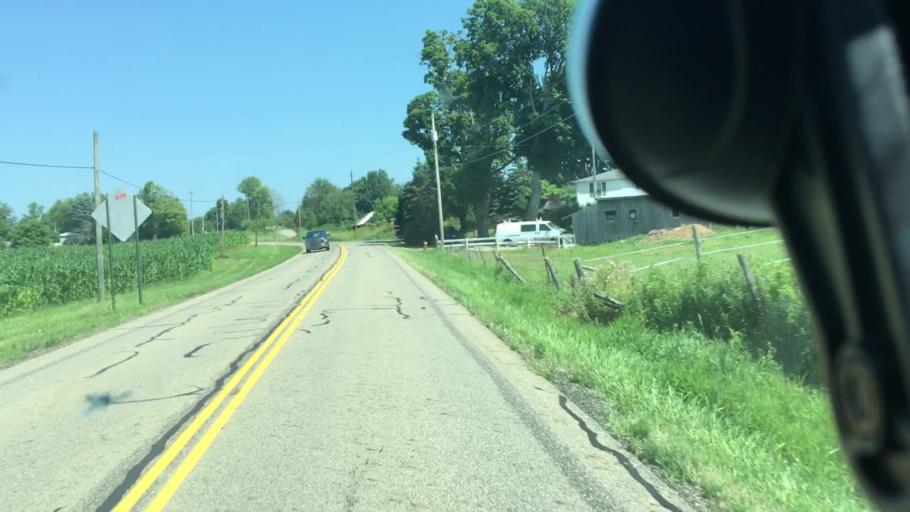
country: US
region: Ohio
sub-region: Columbiana County
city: Lisbon
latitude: 40.7764
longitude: -80.8098
